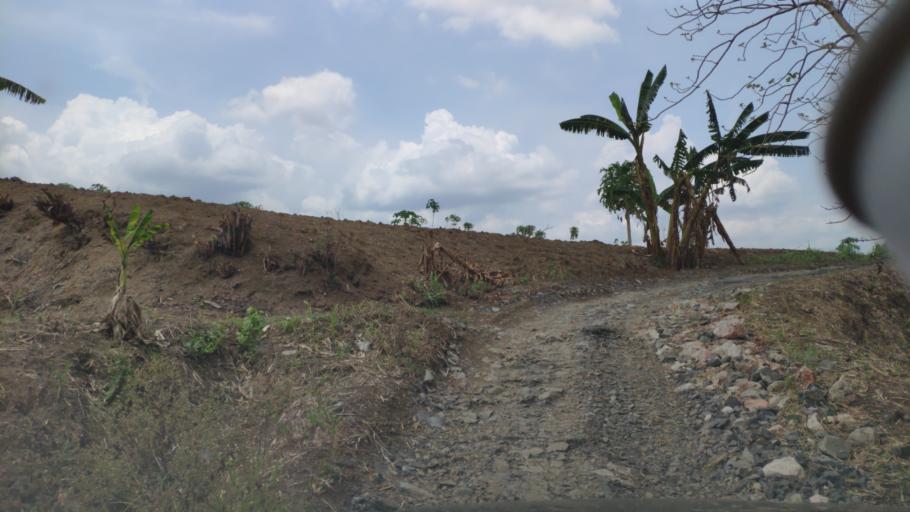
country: ID
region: Central Java
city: Gumiring
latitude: -7.0484
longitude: 111.3924
